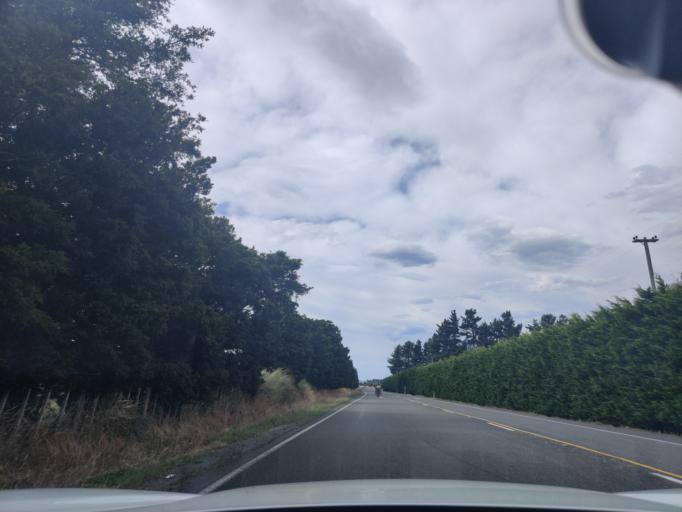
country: NZ
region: Wellington
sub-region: Masterton District
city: Masterton
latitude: -40.8606
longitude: 175.6418
